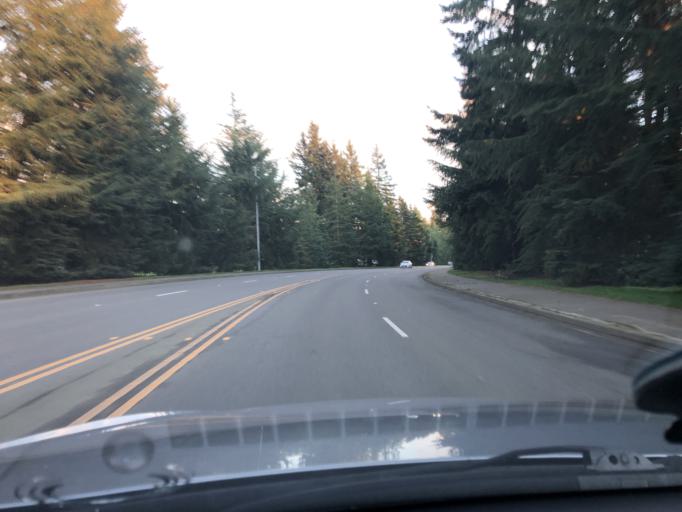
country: US
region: Washington
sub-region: Pierce County
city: Fife Heights
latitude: 47.3151
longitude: -122.3828
